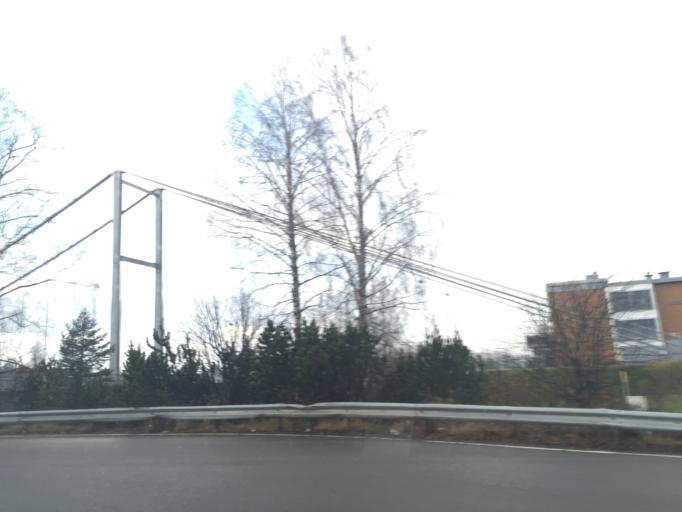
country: NO
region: Hedmark
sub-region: Elverum
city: Elverum
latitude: 60.8831
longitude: 11.5589
